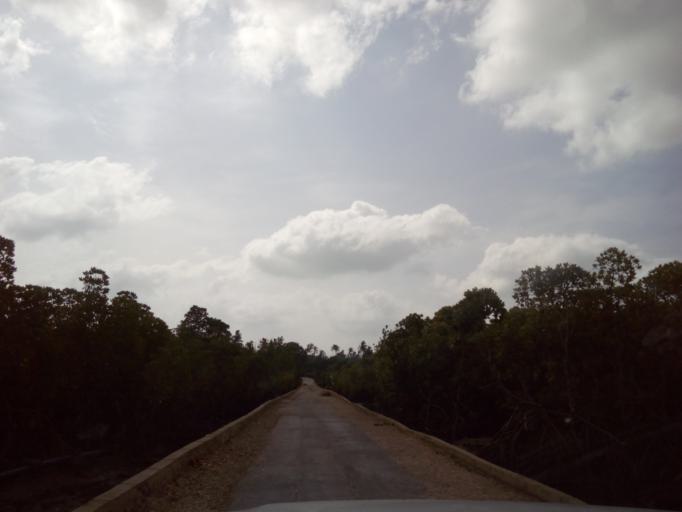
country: TZ
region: Zanzibar Central/South
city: Mahonda
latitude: -6.3229
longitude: 39.3910
